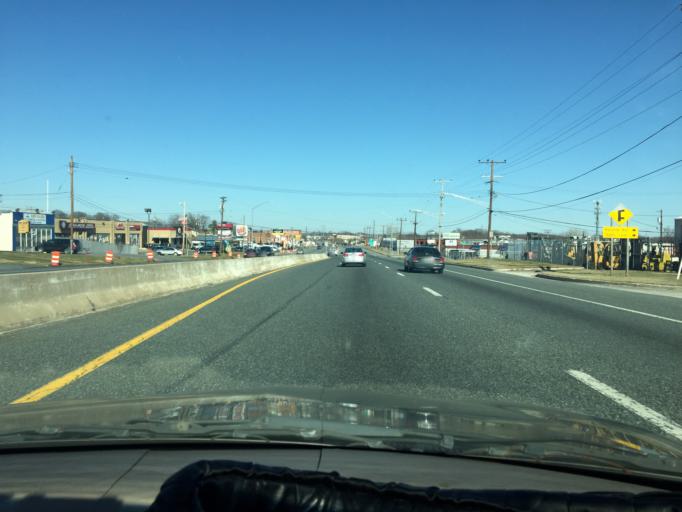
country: US
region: Maryland
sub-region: Baltimore County
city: Rosedale
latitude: 39.3223
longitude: -76.5045
